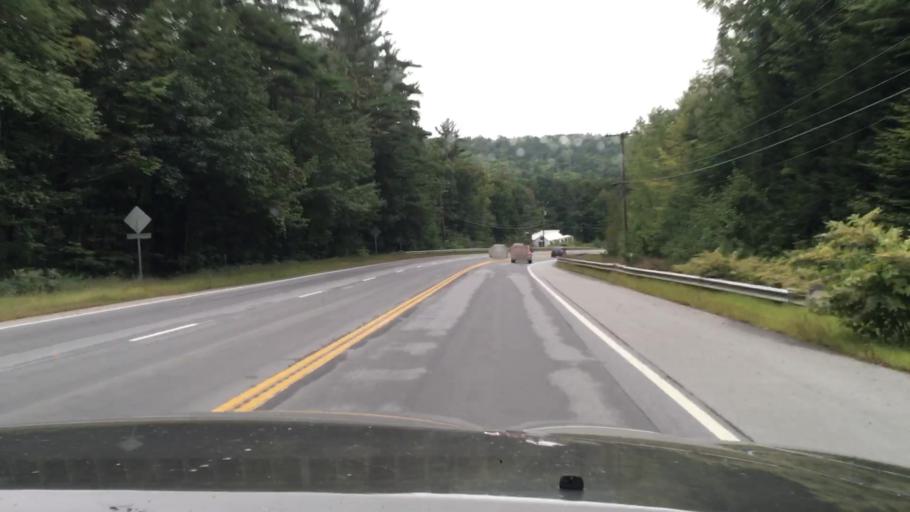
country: US
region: New Hampshire
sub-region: Cheshire County
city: Chesterfield
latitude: 42.8932
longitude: -72.4947
